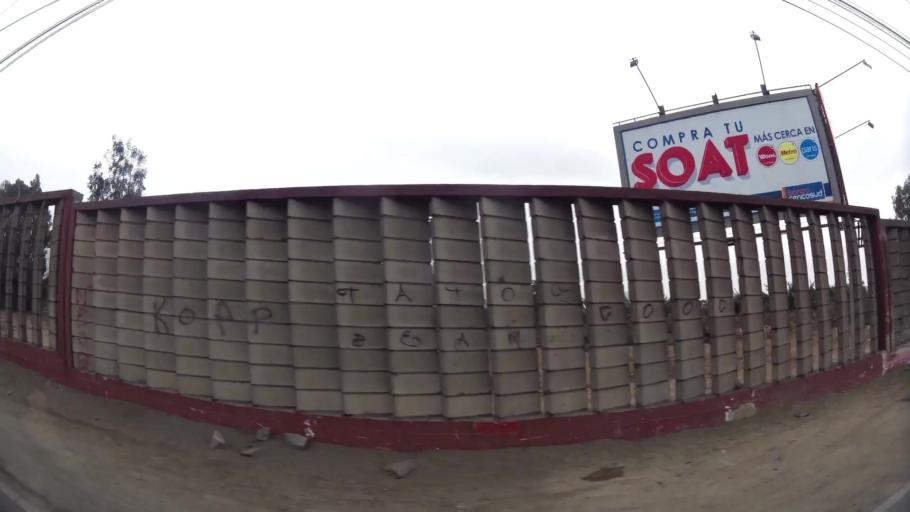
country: PE
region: Lima
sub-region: Lima
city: La Molina
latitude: -12.0774
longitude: -76.9332
